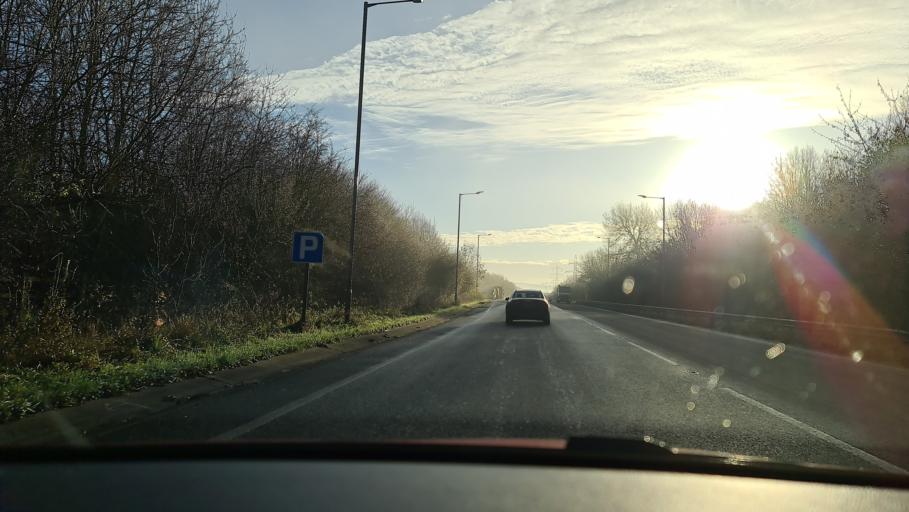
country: GB
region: England
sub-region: Buckinghamshire
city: Weston Turville
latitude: 51.7694
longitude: -0.7636
